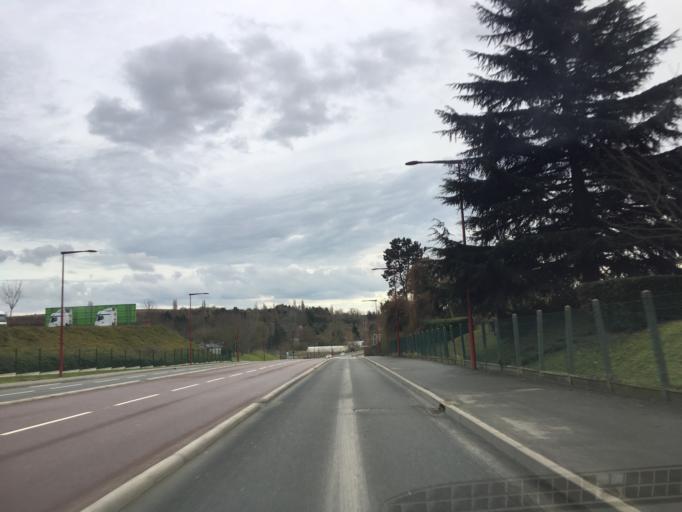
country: FR
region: Ile-de-France
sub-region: Departement du Val-d'Oise
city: Gonesse
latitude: 48.9903
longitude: 2.4573
